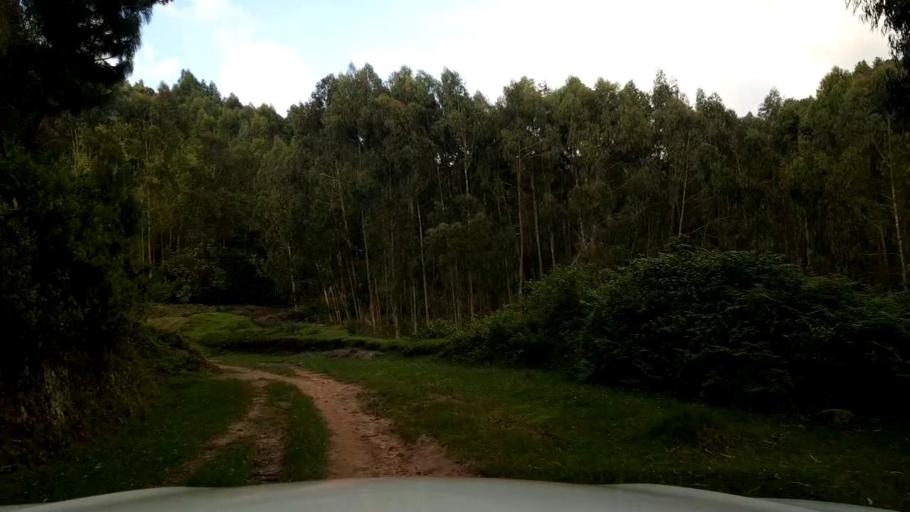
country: RW
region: Western Province
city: Gisenyi
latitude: -1.7238
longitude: 29.4365
